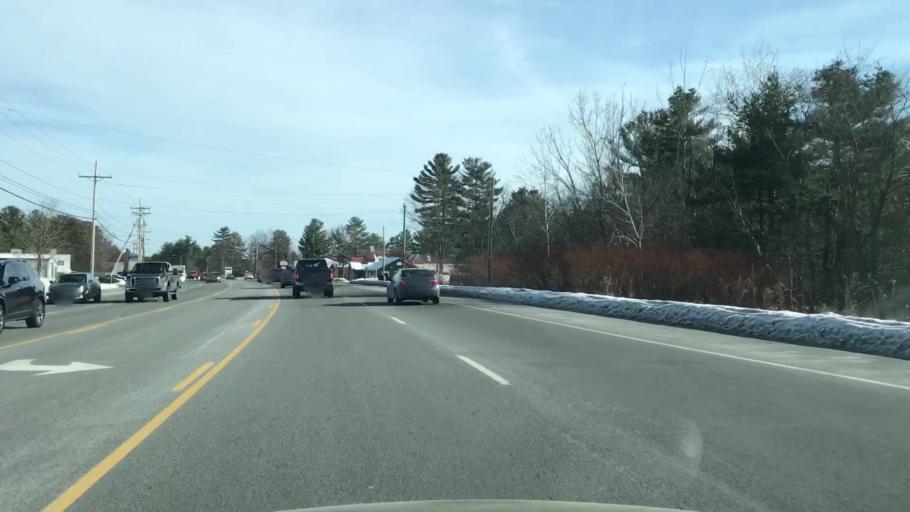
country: US
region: New Hampshire
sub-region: Hillsborough County
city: Milford
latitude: 42.8115
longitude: -71.5894
